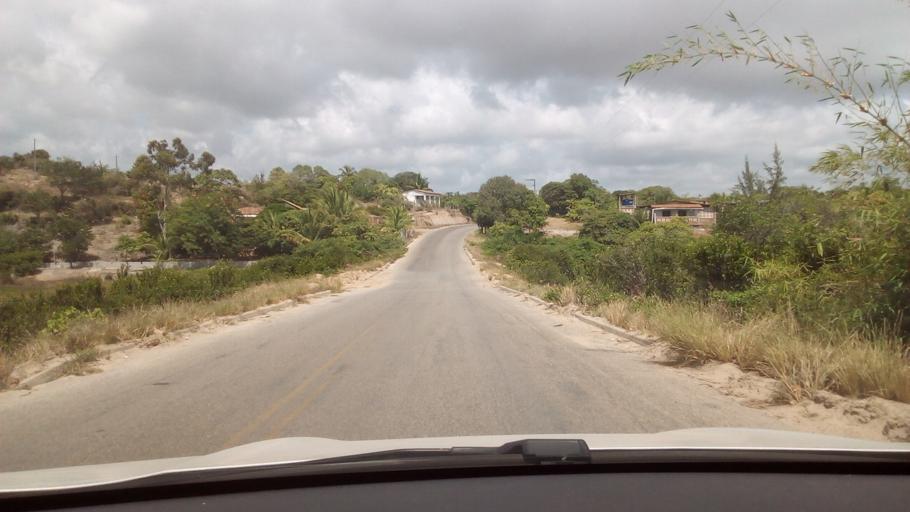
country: BR
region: Paraiba
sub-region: Conde
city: Conde
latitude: -7.3139
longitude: -34.8078
